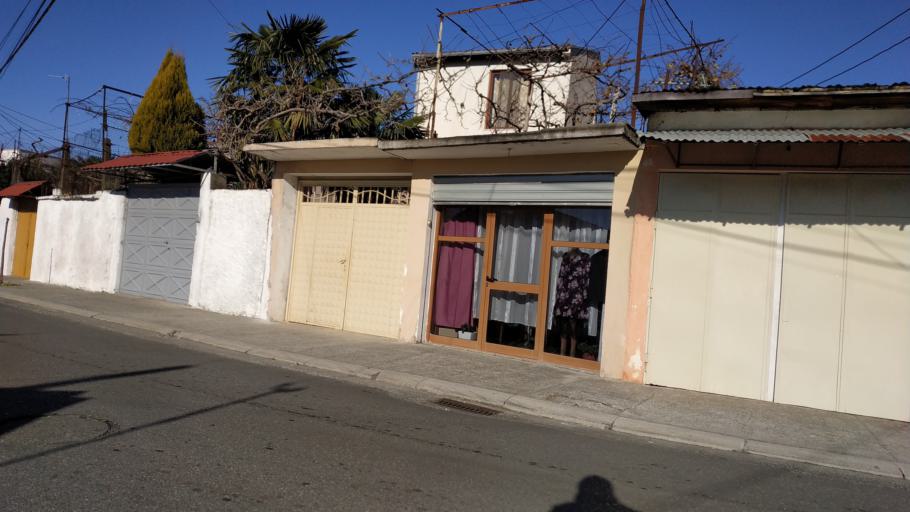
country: AL
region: Shkoder
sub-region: Rrethi i Shkodres
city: Shkoder
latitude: 42.0672
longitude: 19.5035
